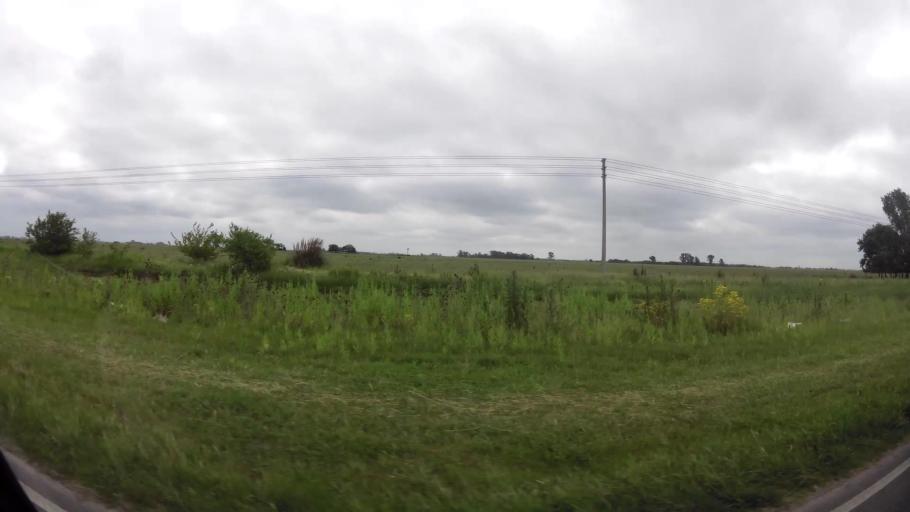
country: AR
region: Buenos Aires
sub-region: Partido de San Vicente
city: San Vicente
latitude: -35.0042
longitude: -58.4698
